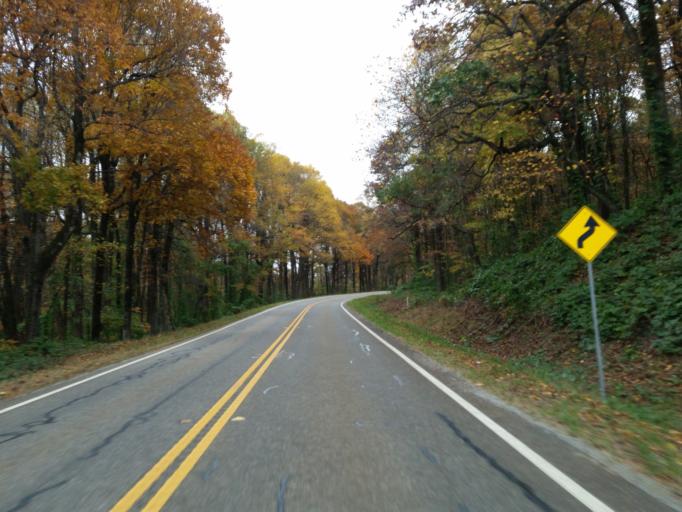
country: US
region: Georgia
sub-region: Pickens County
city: Jasper
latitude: 34.5419
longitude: -84.3533
